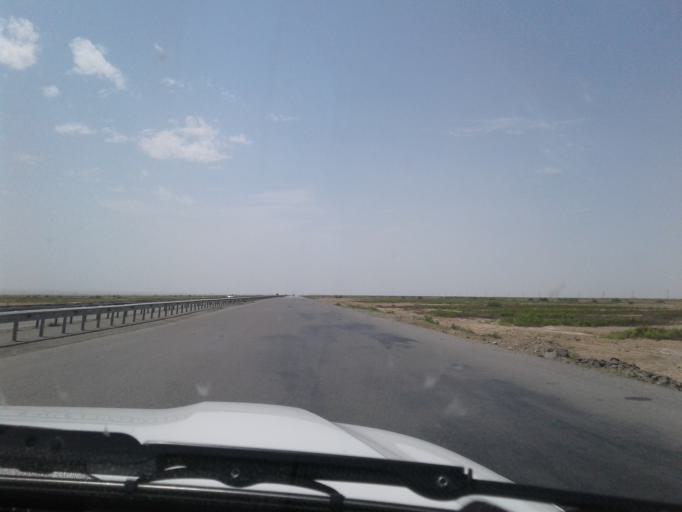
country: IR
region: Razavi Khorasan
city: Kalat-e Naderi
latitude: 37.2152
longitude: 60.0002
